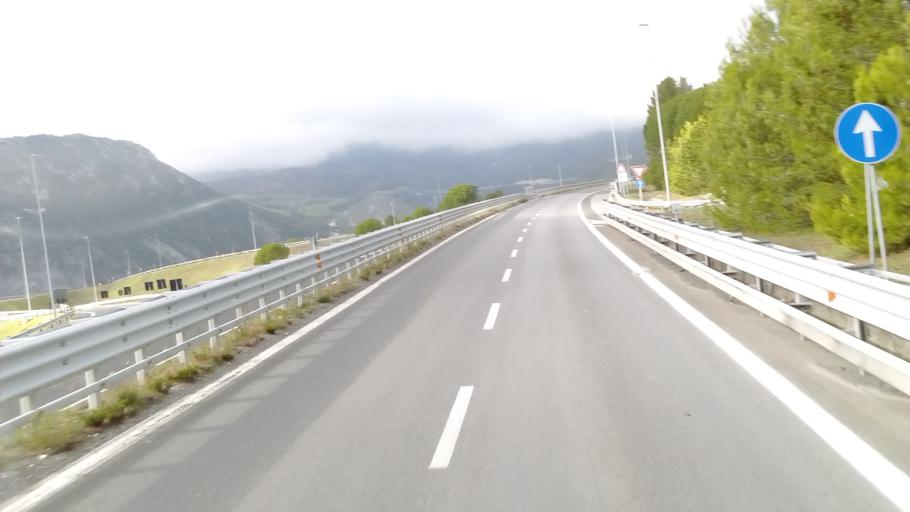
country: IT
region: Calabria
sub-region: Provincia di Cosenza
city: Morano Calabro
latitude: 39.8740
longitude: 16.1696
